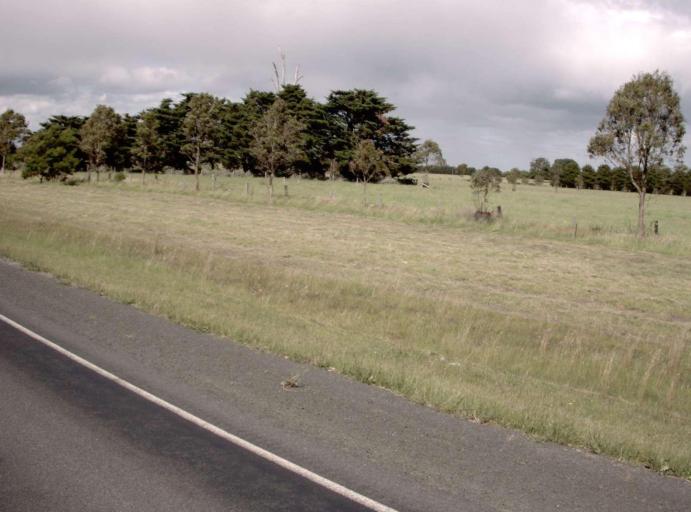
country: AU
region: Victoria
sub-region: Latrobe
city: Traralgon
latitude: -38.1427
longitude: 146.5275
